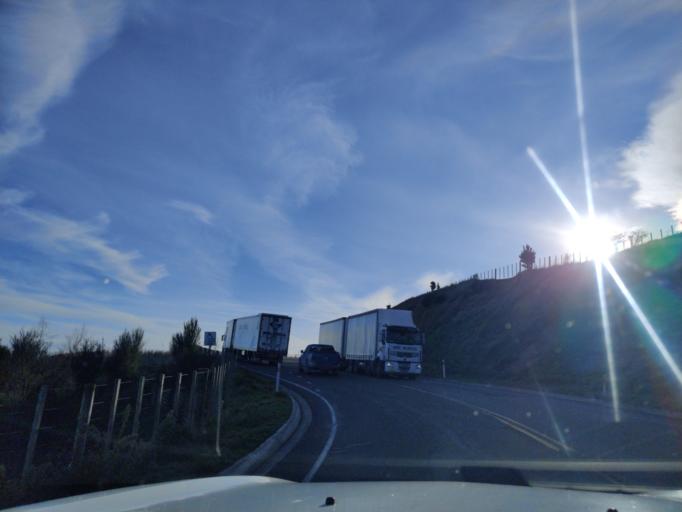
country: NZ
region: Manawatu-Wanganui
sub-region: Palmerston North City
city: Palmerston North
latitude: -40.2873
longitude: 175.7866
